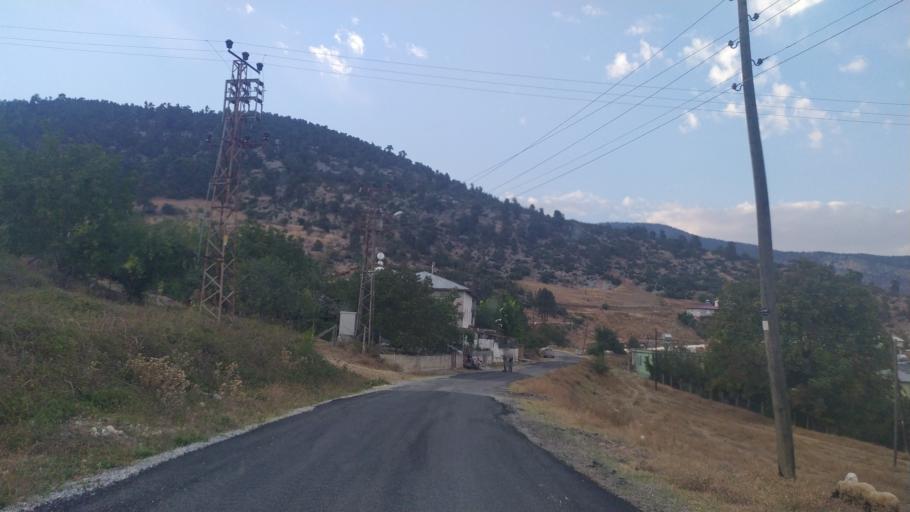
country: TR
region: Mersin
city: Camliyayla
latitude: 37.2287
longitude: 34.7102
